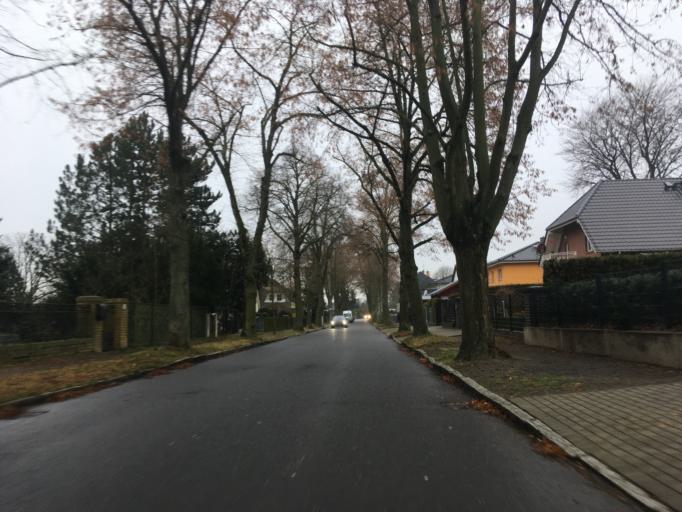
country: DE
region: Berlin
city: Buch
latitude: 52.6332
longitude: 13.5202
